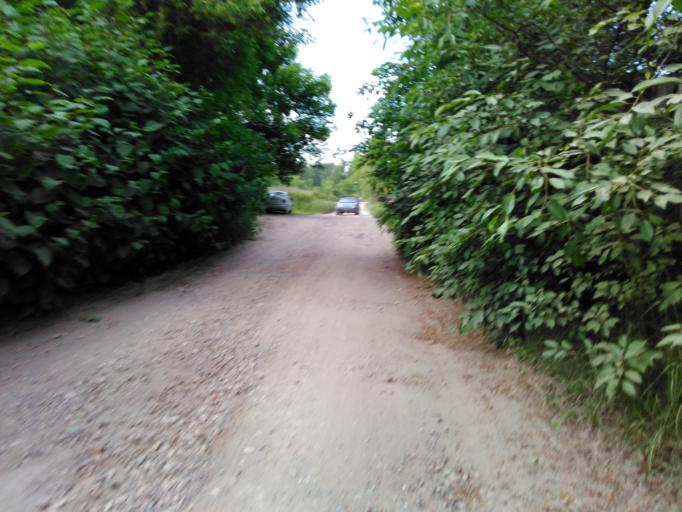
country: RU
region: Moskovskaya
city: Vishnyakovskiye Dachi
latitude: 55.7617
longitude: 38.1419
